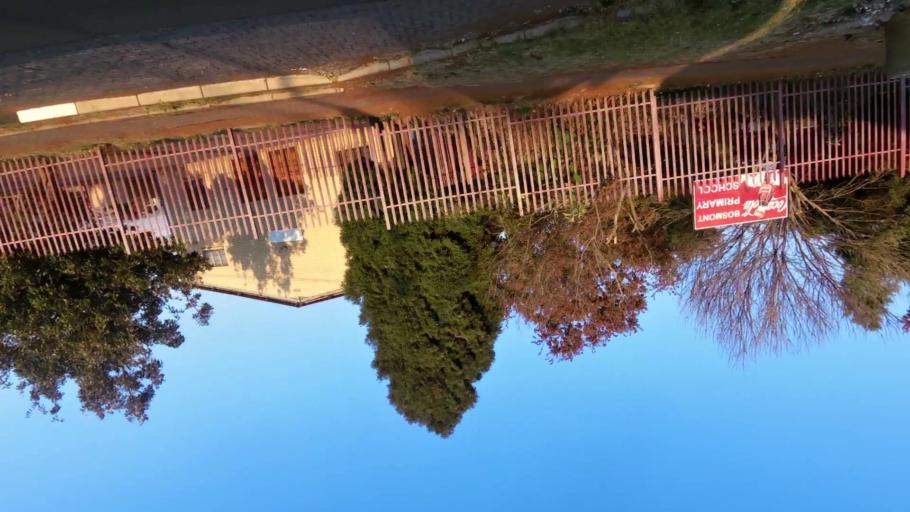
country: ZA
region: Gauteng
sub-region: City of Johannesburg Metropolitan Municipality
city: Roodepoort
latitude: -26.1848
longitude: 27.9501
